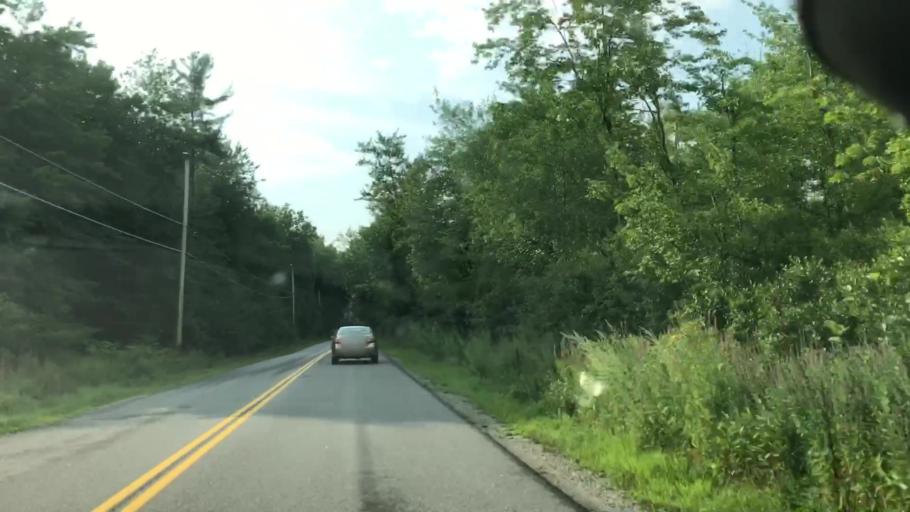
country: US
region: New Hampshire
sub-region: Hillsborough County
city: Milford
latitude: 42.8392
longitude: -71.6008
